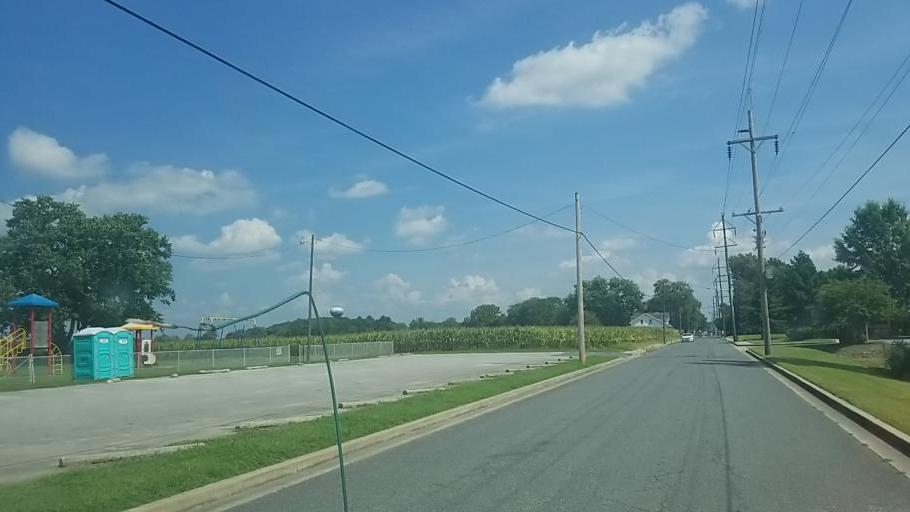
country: US
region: Maryland
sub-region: Wicomico County
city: Hebron
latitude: 38.4219
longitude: -75.6926
